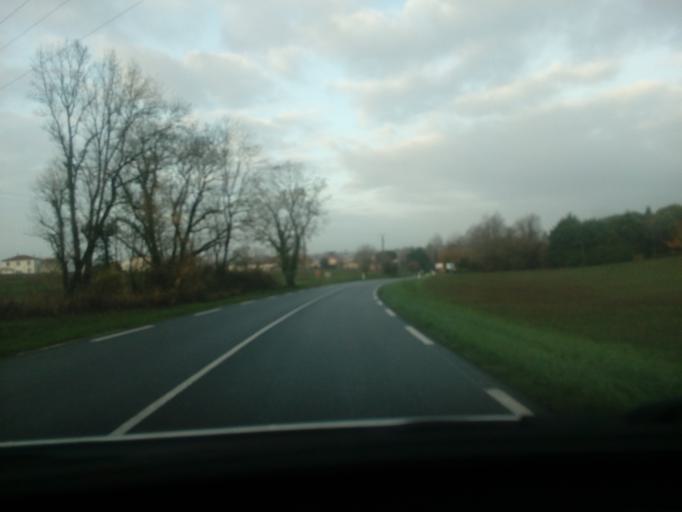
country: FR
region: Poitou-Charentes
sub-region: Departement de la Charente-Maritime
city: Jonzac
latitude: 45.4434
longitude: -0.4197
